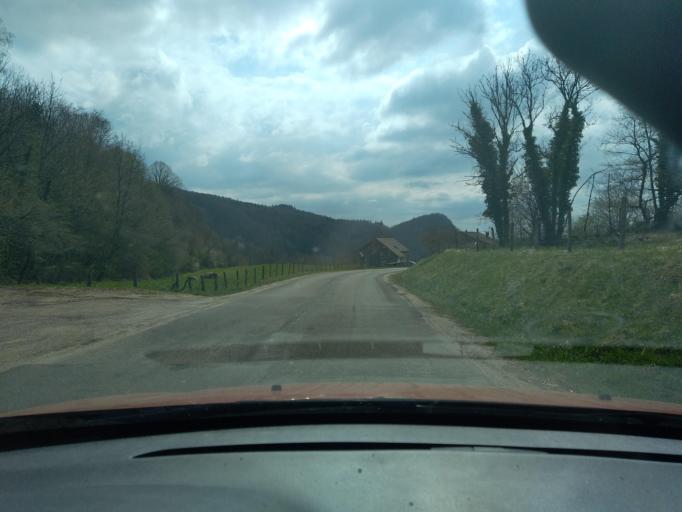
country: FR
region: Franche-Comte
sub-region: Departement du Jura
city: Moirans-en-Montagne
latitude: 46.4630
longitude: 5.7401
